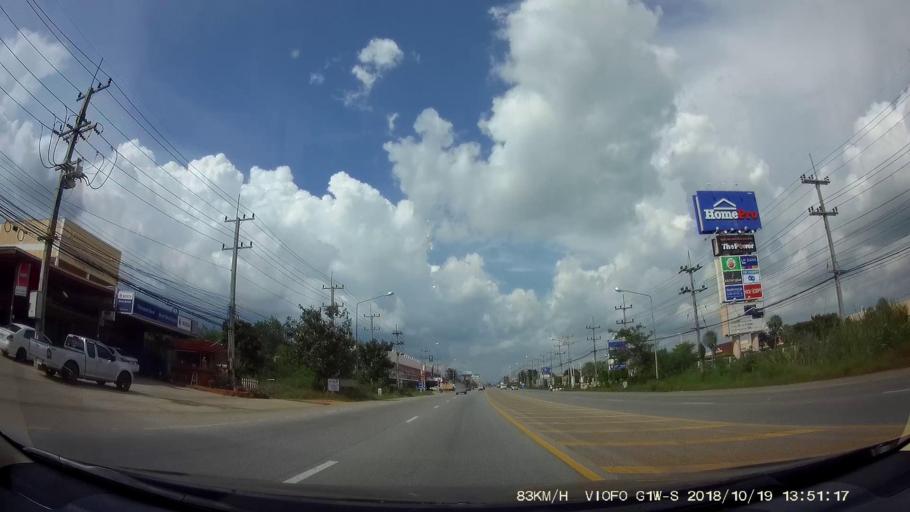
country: TH
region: Chaiyaphum
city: Chaiyaphum
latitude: 15.7545
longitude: 102.0239
